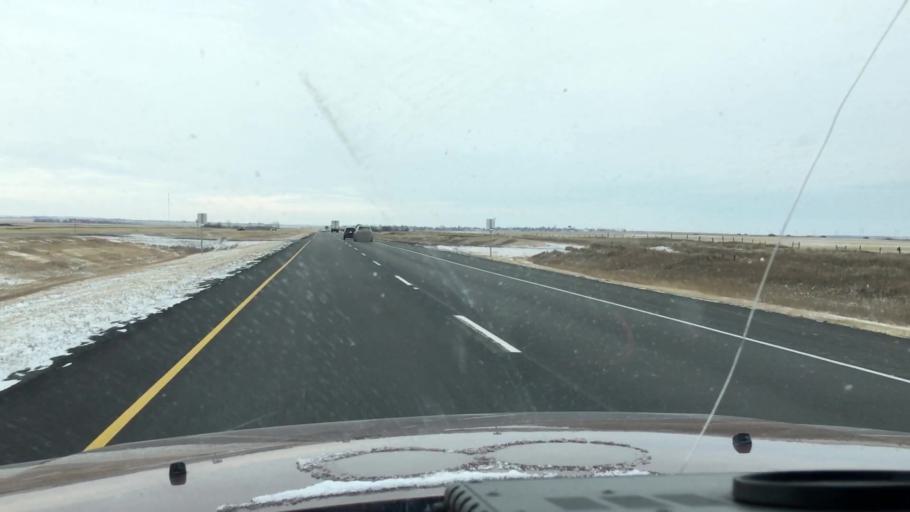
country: CA
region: Saskatchewan
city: Saskatoon
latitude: 51.8391
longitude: -106.5041
